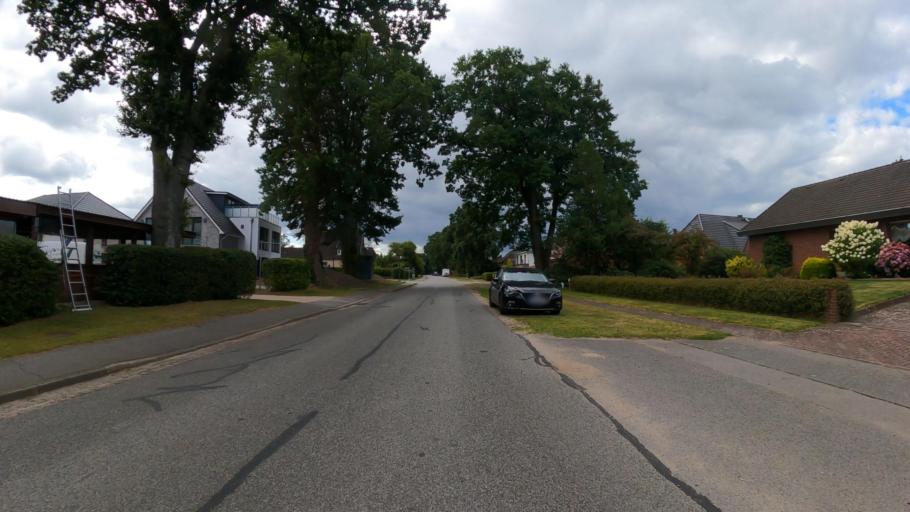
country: DE
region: Schleswig-Holstein
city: Padenstedt
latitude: 54.0479
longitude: 9.9153
